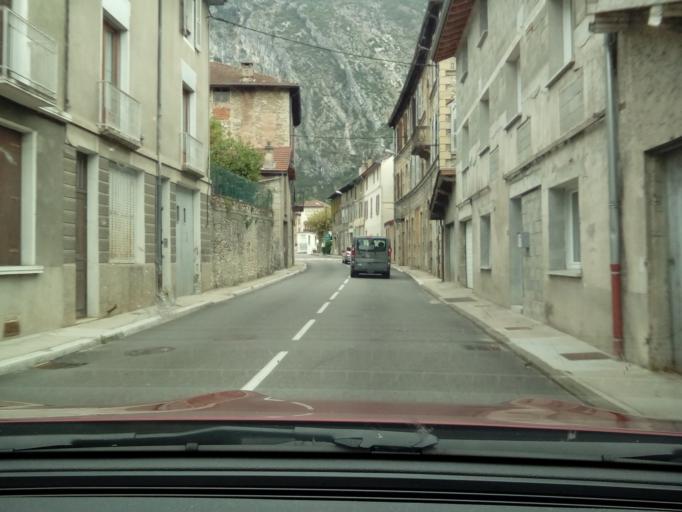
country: FR
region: Rhone-Alpes
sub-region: Departement de l'Isere
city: Pont-en-Royans
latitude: 45.0626
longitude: 5.3403
